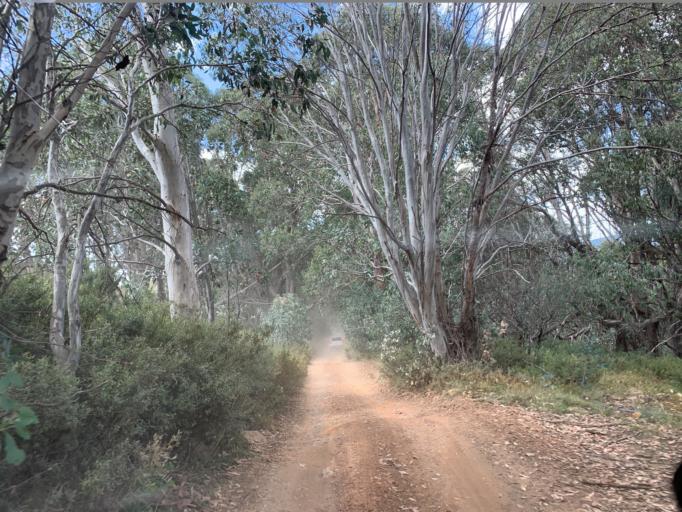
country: AU
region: Victoria
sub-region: Mansfield
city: Mansfield
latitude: -37.1098
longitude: 146.5333
